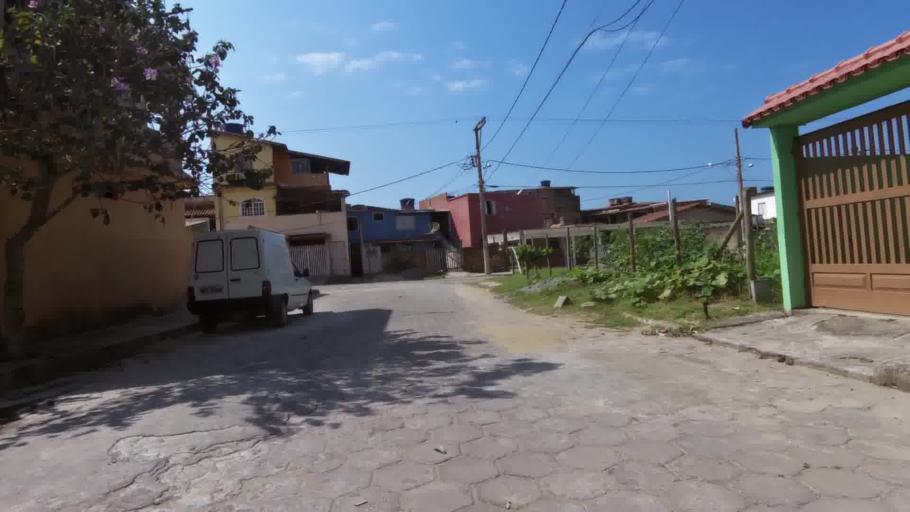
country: BR
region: Espirito Santo
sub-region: Marataizes
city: Marataizes
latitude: -21.0318
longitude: -40.8138
